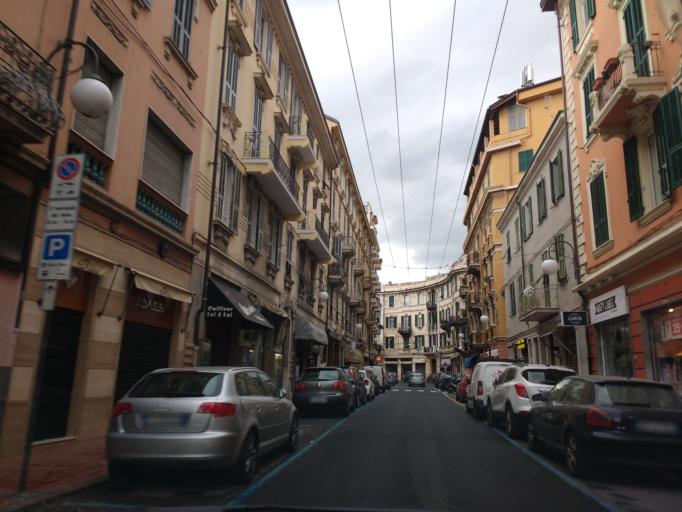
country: IT
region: Liguria
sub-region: Provincia di Imperia
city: Ventimiglia
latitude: 43.7927
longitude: 7.6069
